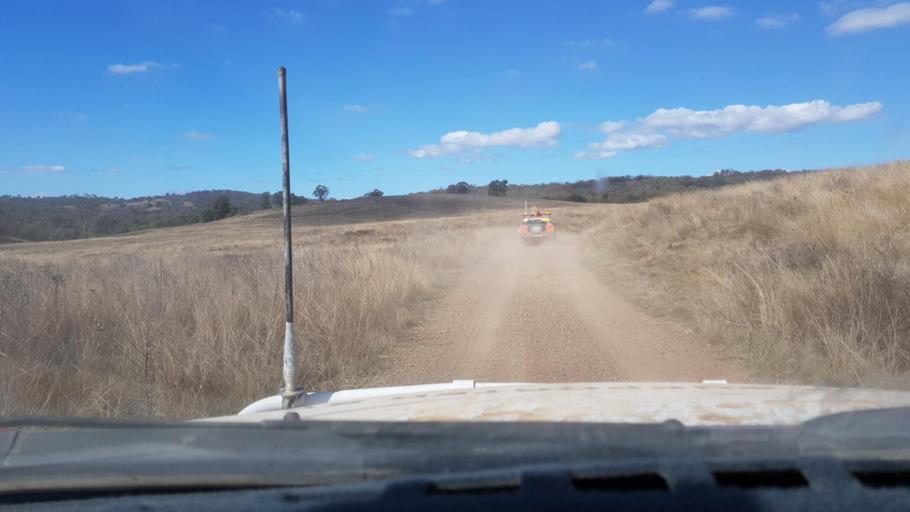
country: AU
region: New South Wales
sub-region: Tamworth Municipality
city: Manilla
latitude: -30.4404
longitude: 150.8621
